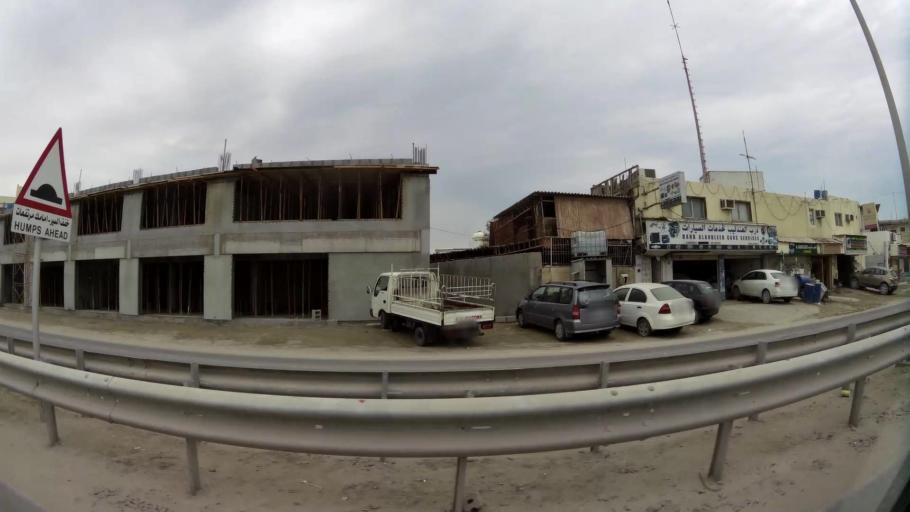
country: BH
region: Northern
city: Sitrah
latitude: 26.1533
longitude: 50.6207
